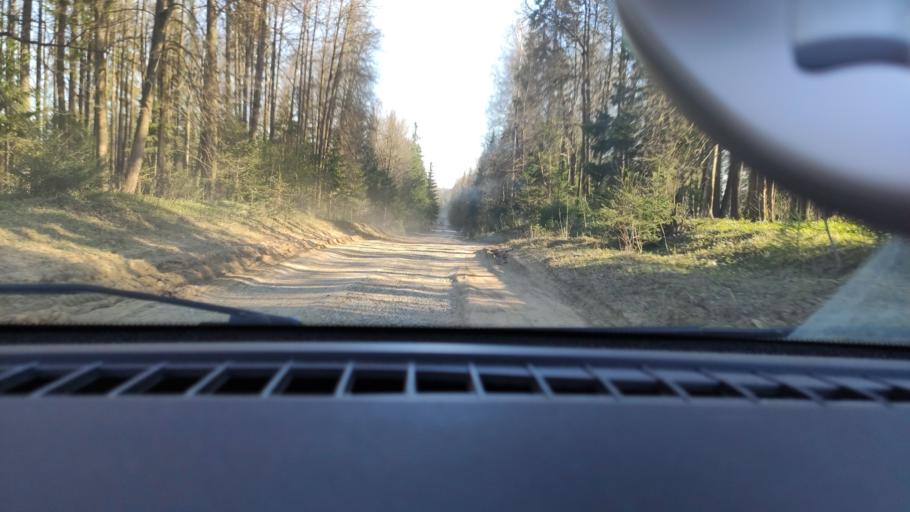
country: RU
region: Perm
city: Polazna
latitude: 58.1325
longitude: 56.4577
